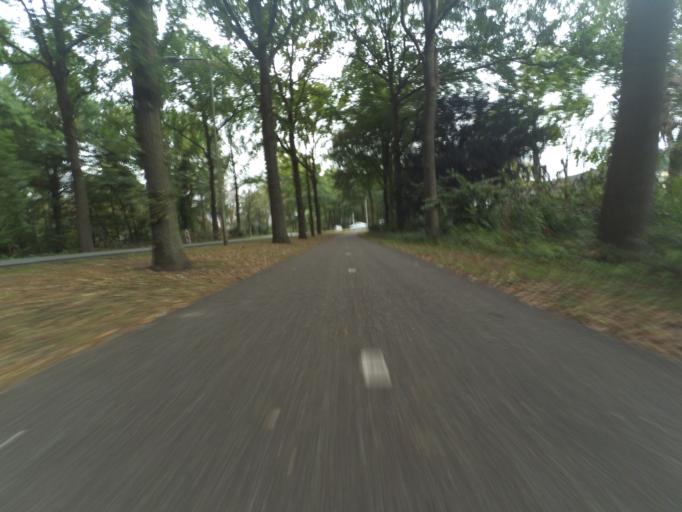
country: NL
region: Gelderland
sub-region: Gemeente Geldermalsen
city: Geldermalsen
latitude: 51.9113
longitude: 5.3308
